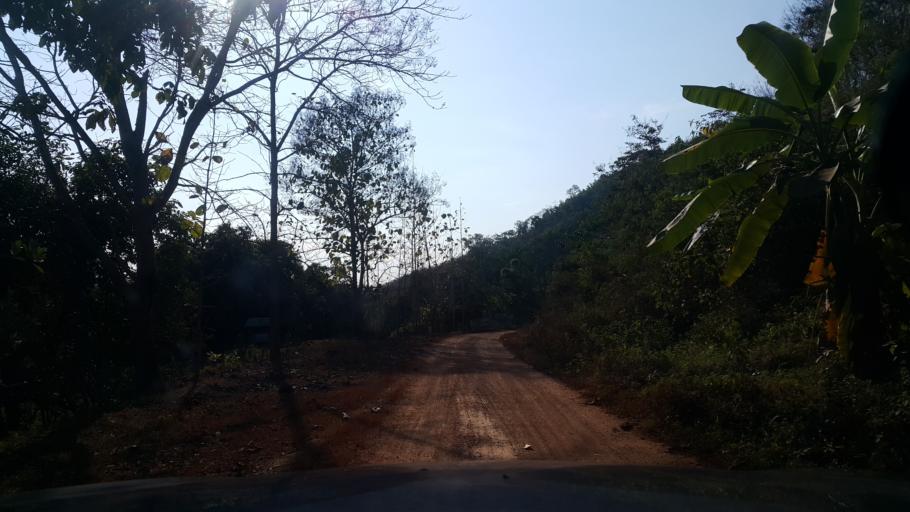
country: TH
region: Loei
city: Chiang Khan
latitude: 17.8315
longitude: 101.6098
